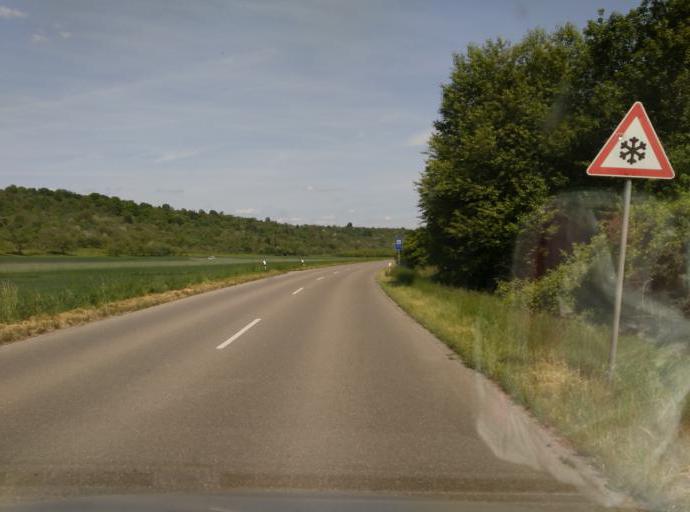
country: DE
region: Baden-Wuerttemberg
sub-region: Regierungsbezirk Stuttgart
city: Neckartailfingen
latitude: 48.6165
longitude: 9.2755
